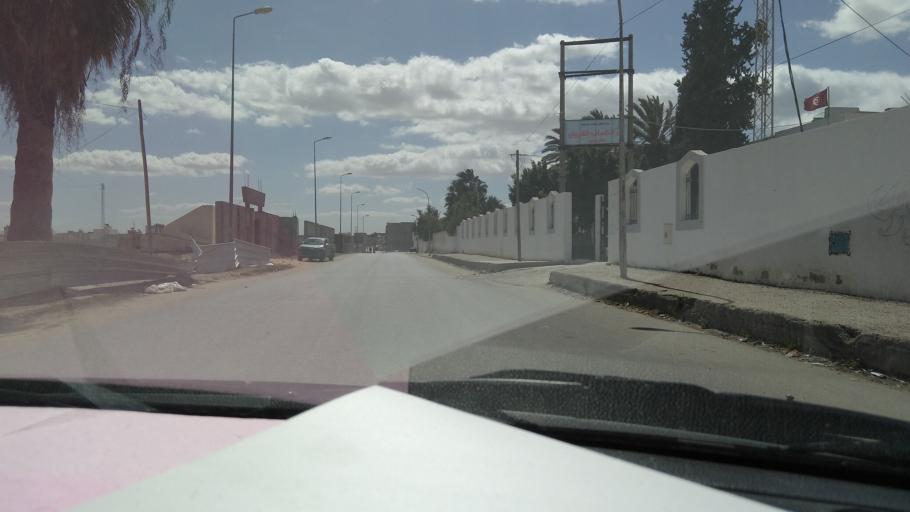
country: TN
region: Al Qayrawan
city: Kairouan
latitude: 35.6665
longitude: 10.1083
